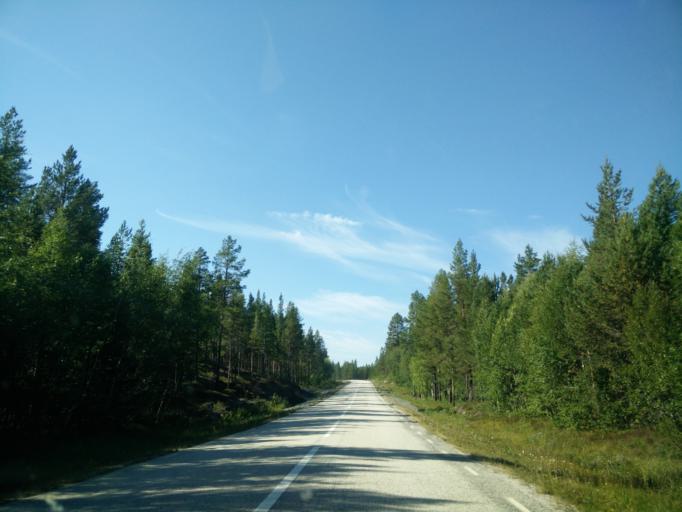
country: SE
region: Jaemtland
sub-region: Are Kommun
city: Jarpen
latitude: 62.8297
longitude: 13.4534
